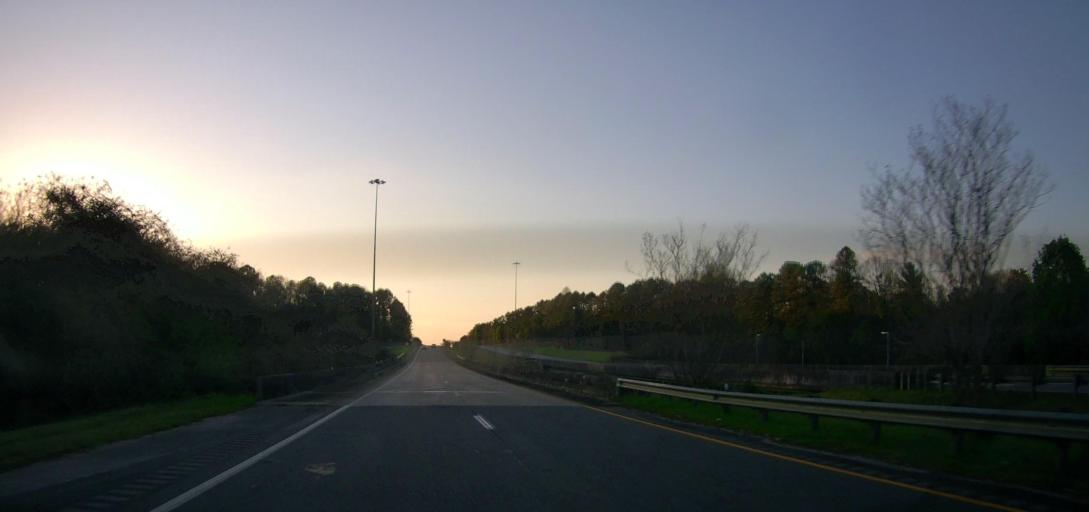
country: US
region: Alabama
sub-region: Talladega County
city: Sylacauga
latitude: 33.1435
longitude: -86.2566
